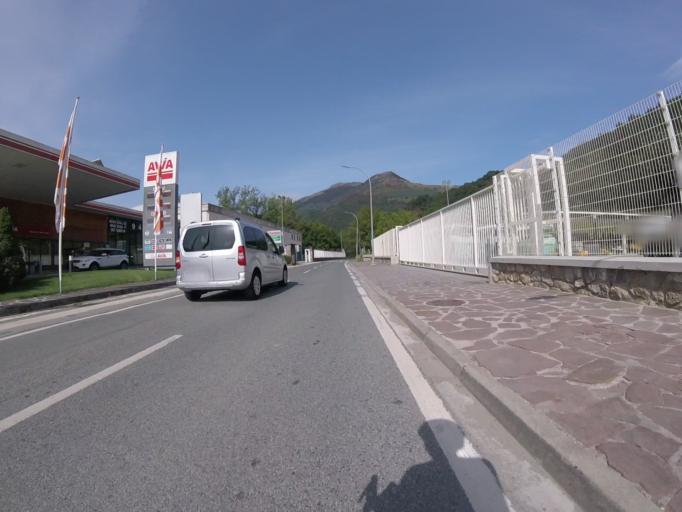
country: ES
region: Navarre
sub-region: Provincia de Navarra
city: Elgorriaga
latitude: 43.1362
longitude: -1.6802
